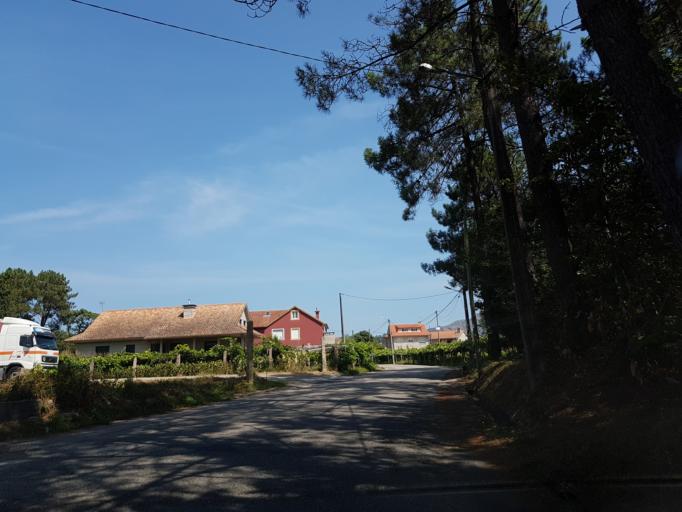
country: ES
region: Galicia
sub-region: Provincia de Pontevedra
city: Porrino
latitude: 42.2088
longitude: -8.6202
